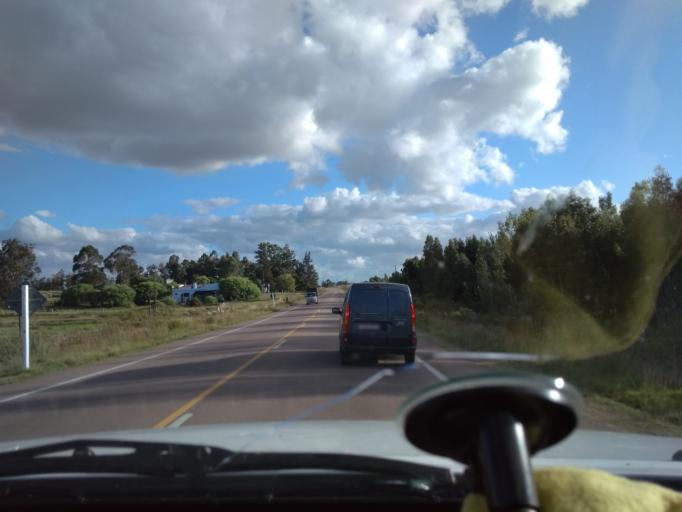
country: UY
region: Canelones
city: San Jacinto
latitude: -34.4618
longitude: -55.8293
